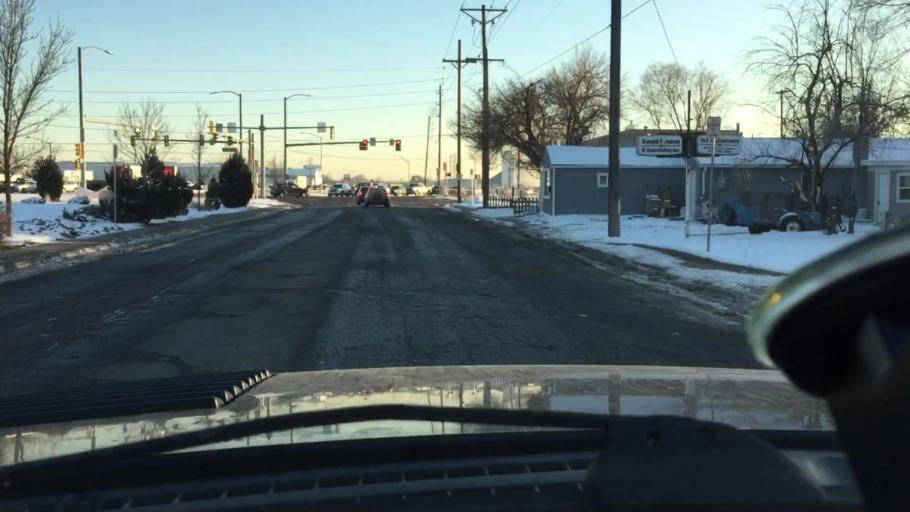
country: US
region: Colorado
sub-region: Adams County
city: Commerce City
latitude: 39.8227
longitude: -104.9316
